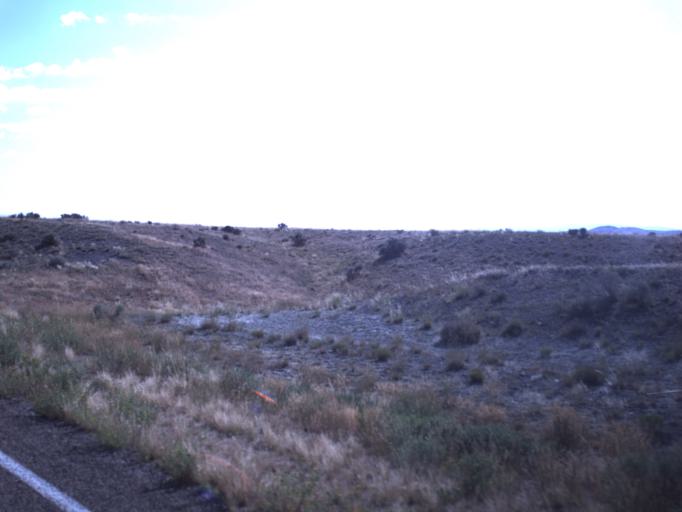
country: US
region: Utah
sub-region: Beaver County
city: Milford
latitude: 38.7673
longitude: -112.9367
